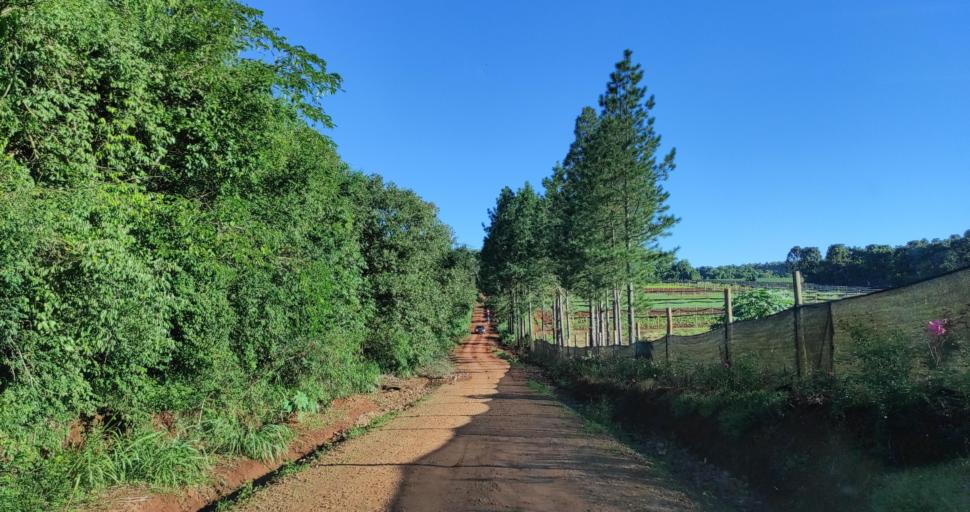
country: AR
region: Misiones
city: Puerto Rico
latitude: -26.8272
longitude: -55.0113
